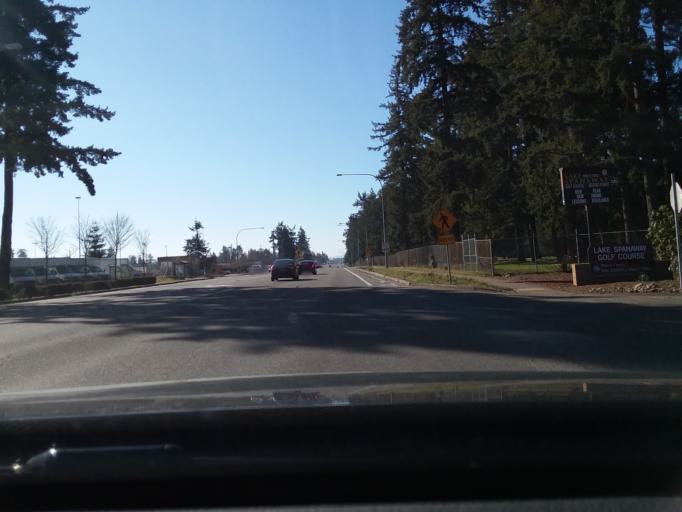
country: US
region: Washington
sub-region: Pierce County
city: Spanaway
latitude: 47.1168
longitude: -122.4350
